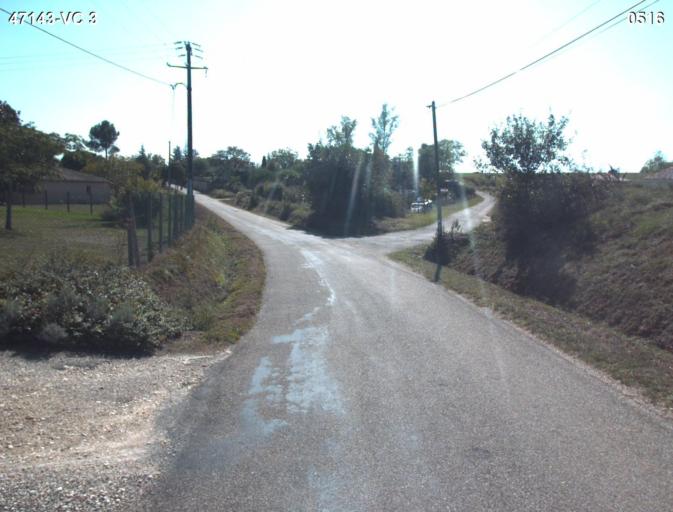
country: FR
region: Aquitaine
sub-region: Departement du Lot-et-Garonne
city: Lavardac
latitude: 44.1881
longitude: 0.2950
